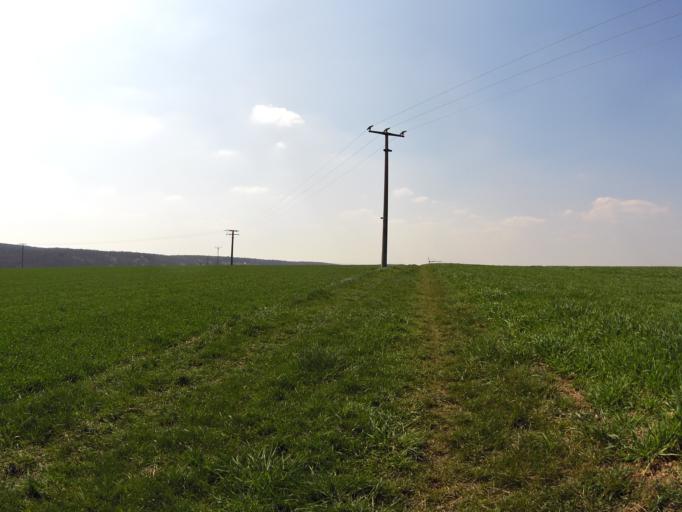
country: DE
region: Bavaria
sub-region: Regierungsbezirk Unterfranken
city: Theilheim
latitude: 49.7585
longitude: 10.0428
